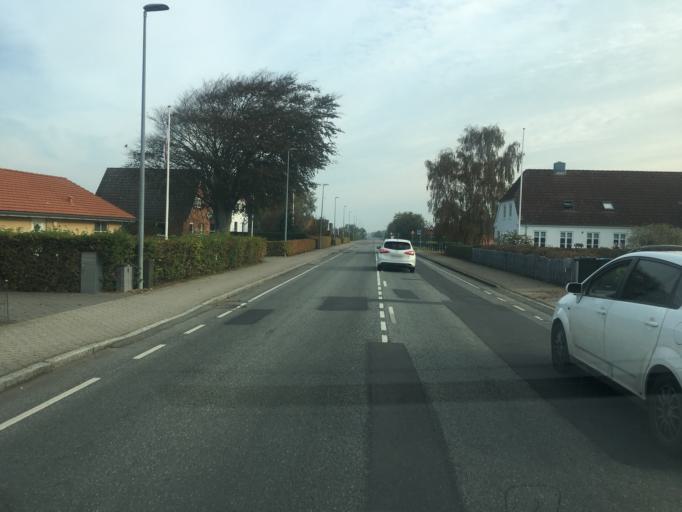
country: DK
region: South Denmark
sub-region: Tonder Kommune
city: Logumkloster
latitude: 55.0647
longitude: 8.9570
